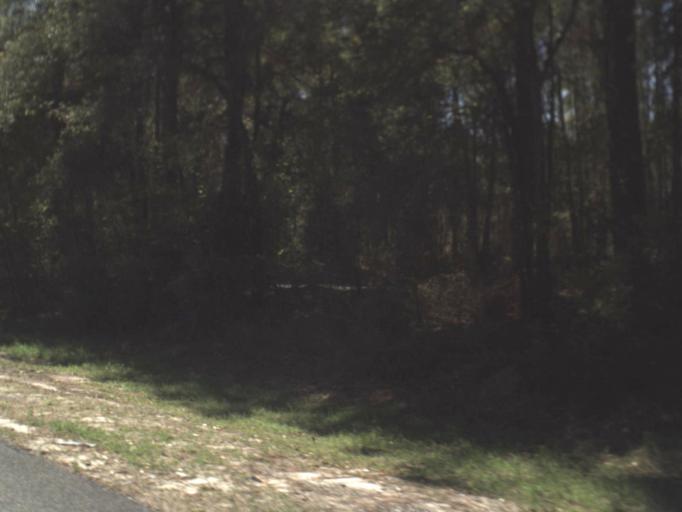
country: US
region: Florida
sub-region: Leon County
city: Woodville
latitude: 30.3663
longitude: -84.2661
